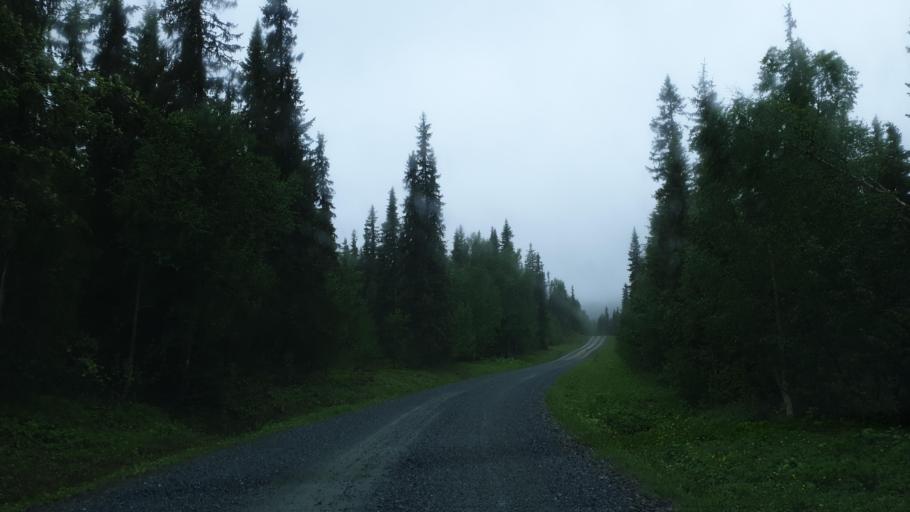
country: SE
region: Vaesterbotten
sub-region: Vilhelmina Kommun
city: Sjoberg
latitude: 65.2742
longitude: 15.9108
